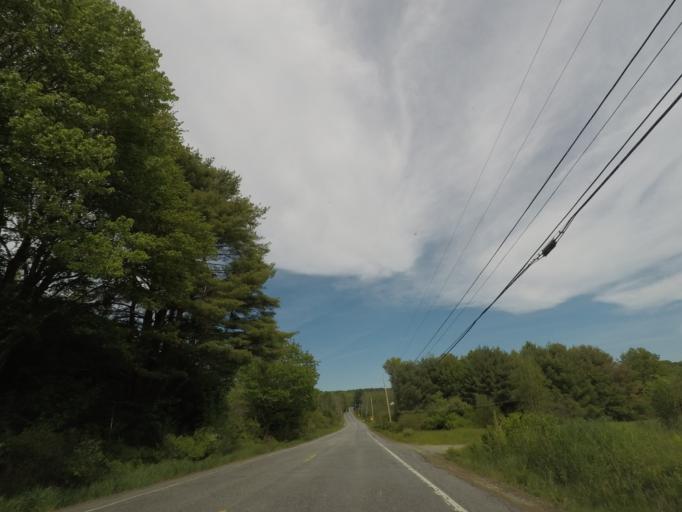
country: US
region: Maine
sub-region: Sagadahoc County
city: Richmond
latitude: 44.0850
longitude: -69.7549
